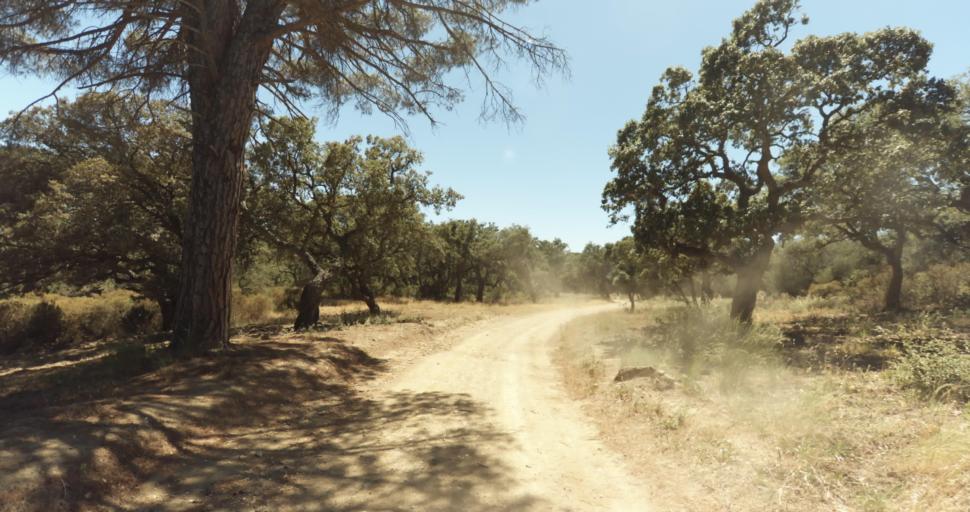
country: FR
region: Provence-Alpes-Cote d'Azur
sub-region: Departement du Var
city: Gassin
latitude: 43.2496
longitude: 6.5634
